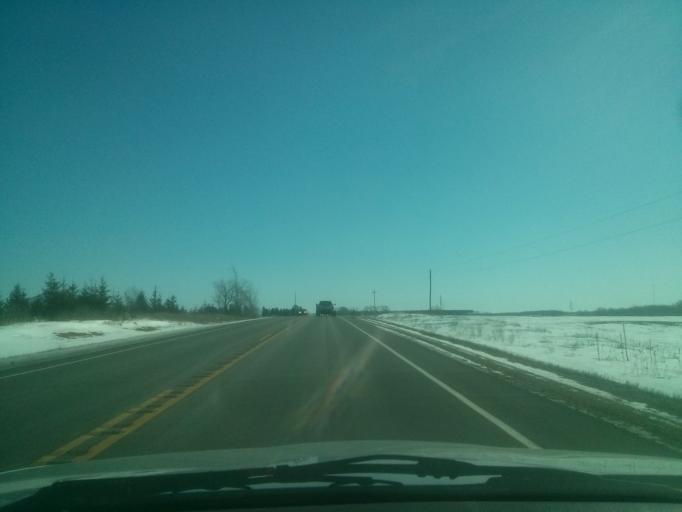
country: US
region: Wisconsin
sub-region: Polk County
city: Clear Lake
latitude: 45.1363
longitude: -92.3079
